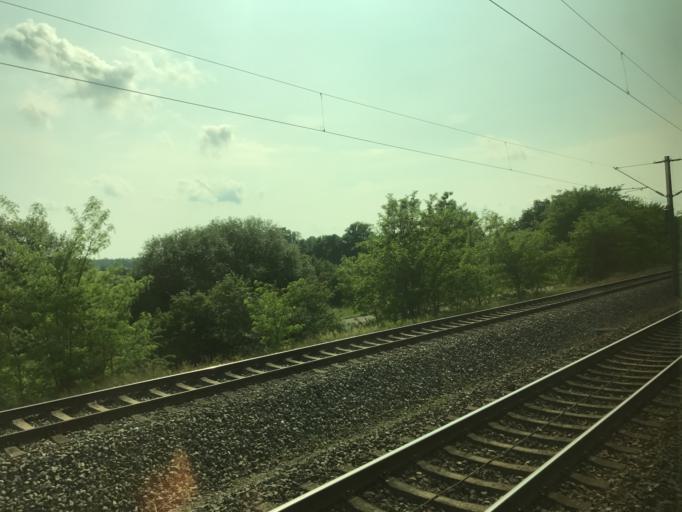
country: DE
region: Brandenburg
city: Nennhausen
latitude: 52.5993
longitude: 12.5146
